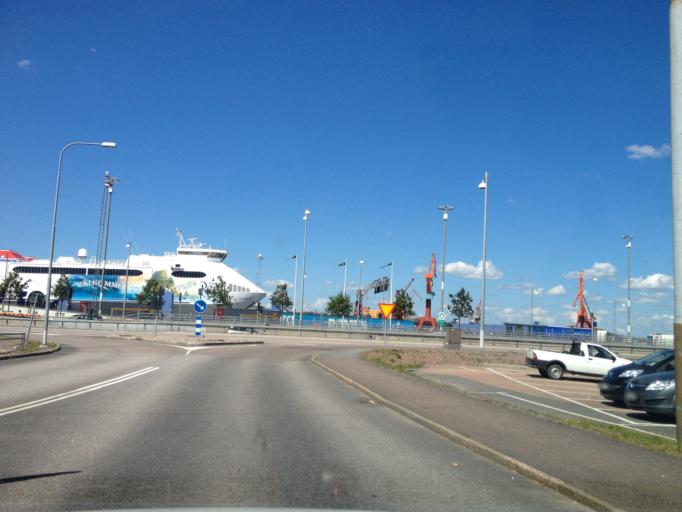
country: SE
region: Vaestra Goetaland
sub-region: Goteborg
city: Goeteborg
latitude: 57.7005
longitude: 11.9489
